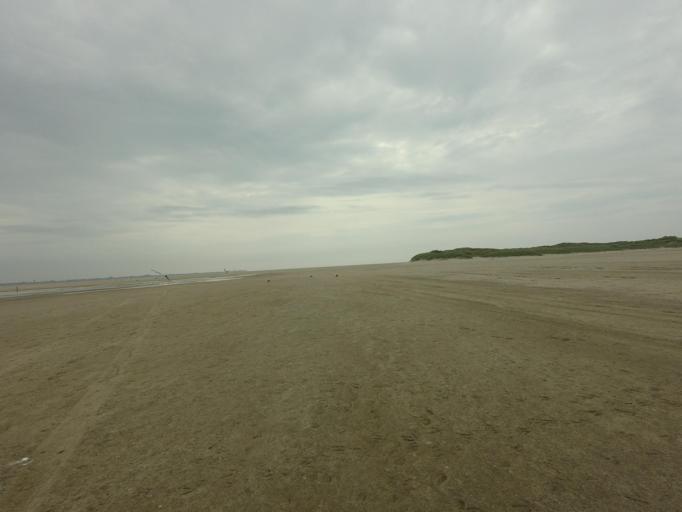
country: NL
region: North Holland
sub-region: Gemeente Den Helder
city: Den Helder
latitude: 52.9947
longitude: 4.7526
